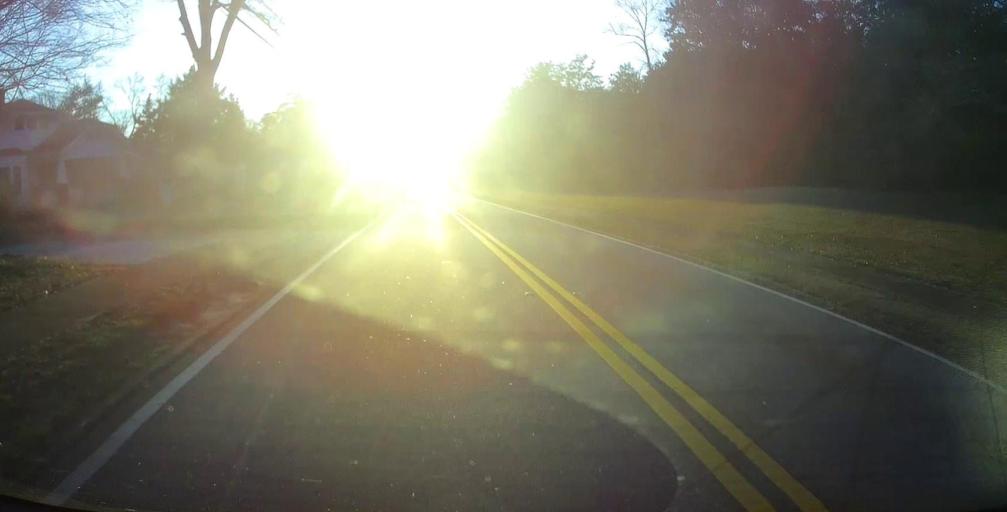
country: US
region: Georgia
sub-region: Troup County
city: La Grange
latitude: 33.0363
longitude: -85.0497
